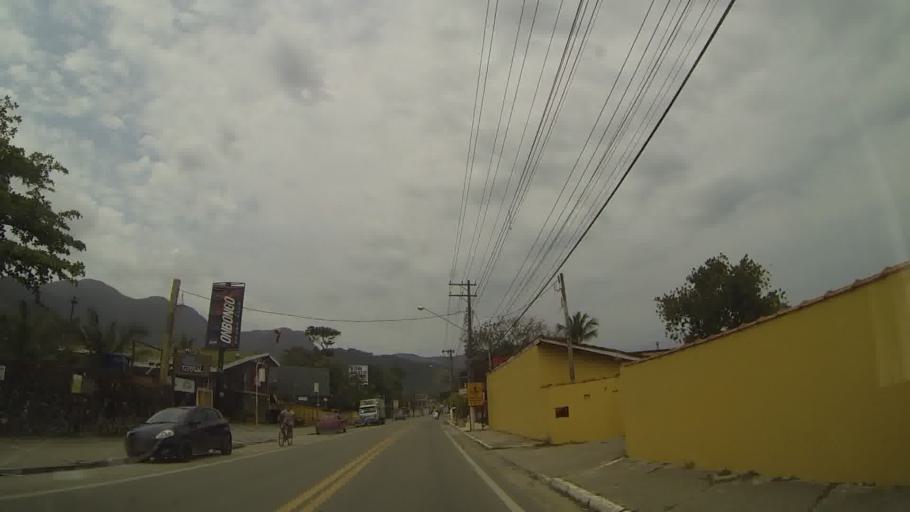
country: BR
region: Sao Paulo
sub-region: Sao Sebastiao
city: Sao Sebastiao
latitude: -23.7912
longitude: -45.5608
